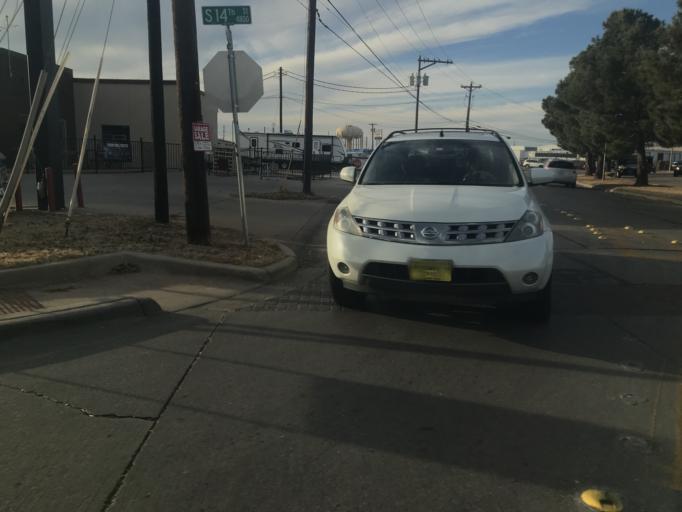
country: US
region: Texas
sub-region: Taylor County
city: Abilene
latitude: 32.4288
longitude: -99.7843
